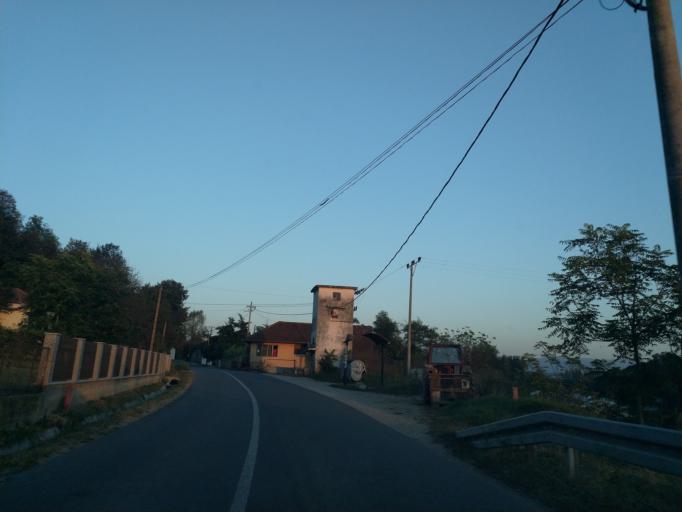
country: RS
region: Central Serbia
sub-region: Rasinski Okrug
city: Krusevac
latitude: 43.6031
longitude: 21.2318
